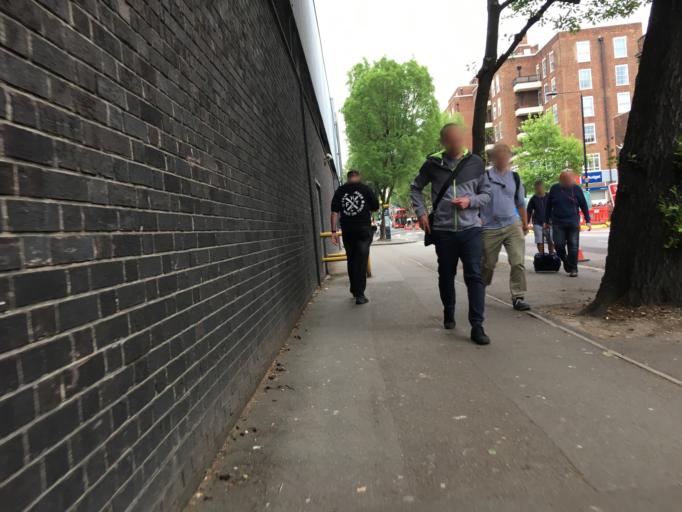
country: GB
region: England
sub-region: Greater London
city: Camden Town
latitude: 51.5297
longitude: -0.1333
